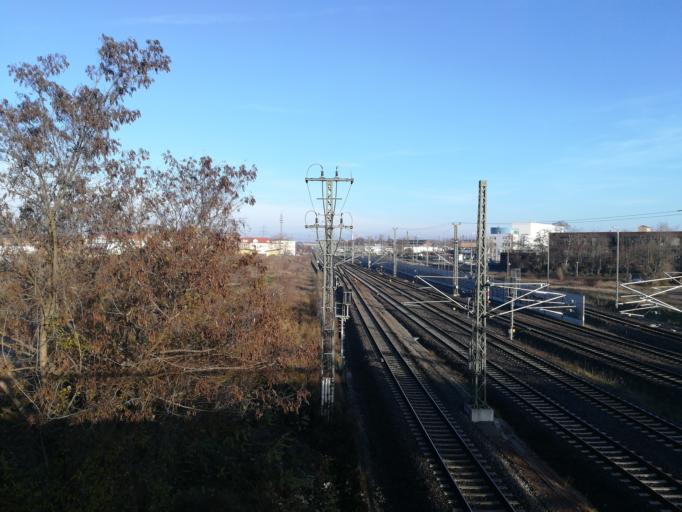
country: DE
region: Saxony-Anhalt
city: Schkopau
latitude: 51.4296
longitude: 11.9876
